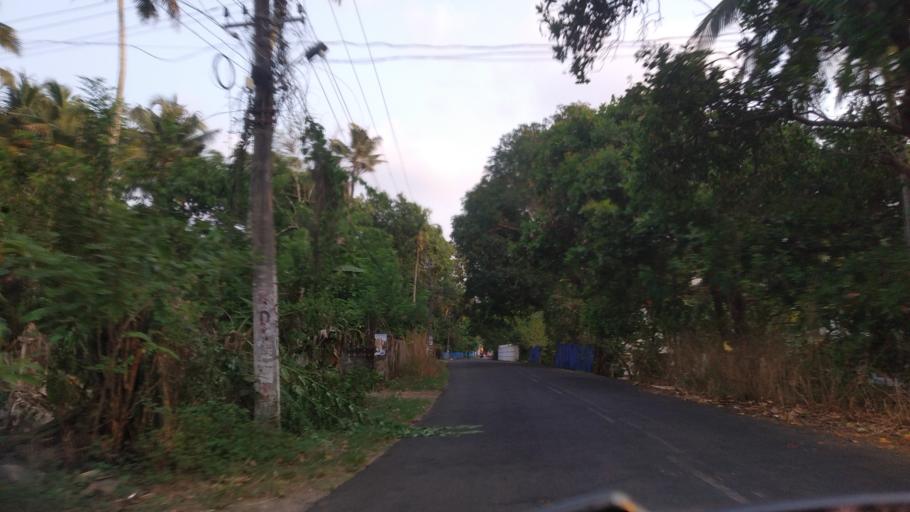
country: IN
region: Kerala
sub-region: Thrissur District
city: Thanniyam
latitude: 10.3436
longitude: 76.1161
